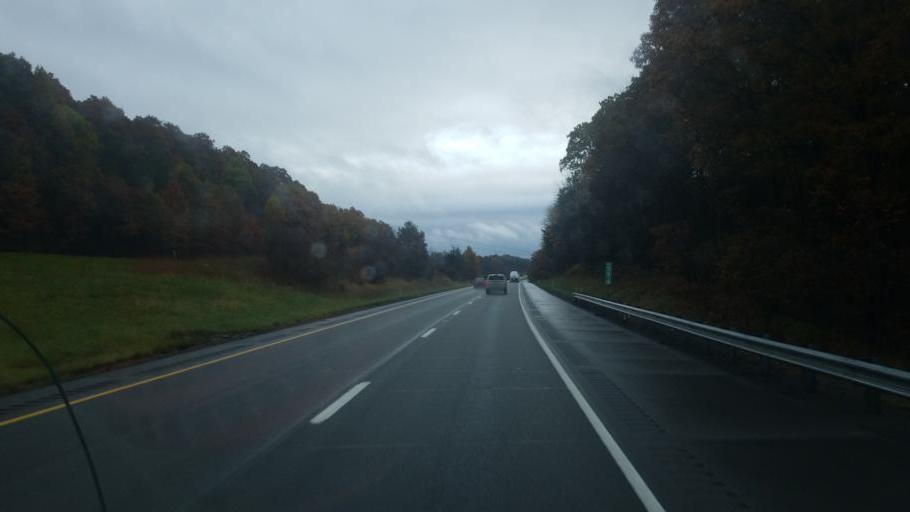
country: US
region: Pennsylvania
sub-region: Clarion County
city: Marianne
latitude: 41.1957
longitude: -79.4393
